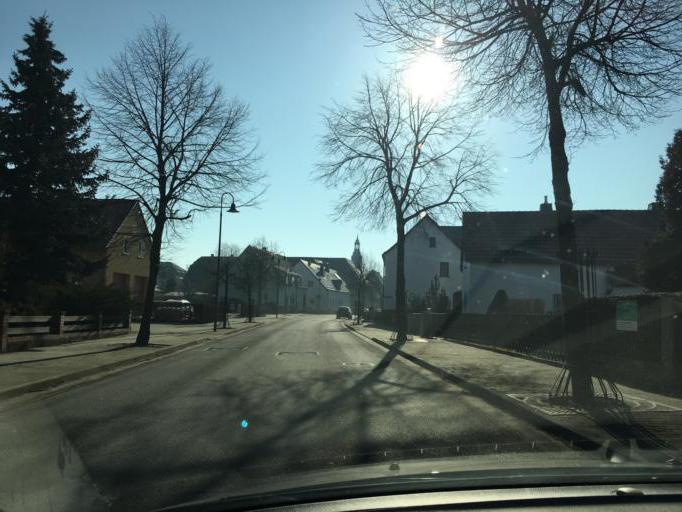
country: DE
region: Saxony
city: Otterwisch
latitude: 51.2060
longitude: 12.6073
